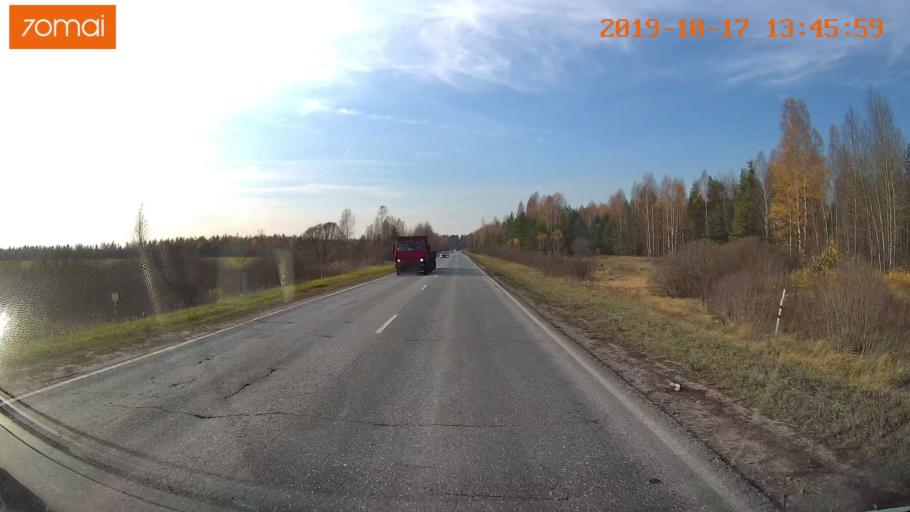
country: RU
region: Rjazan
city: Tuma
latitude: 55.1473
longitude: 40.5012
